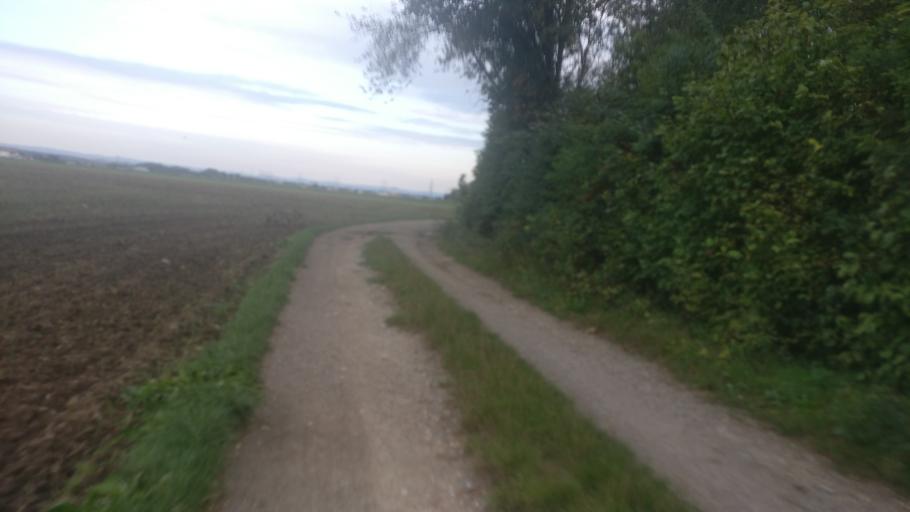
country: AT
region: Lower Austria
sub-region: Politischer Bezirk Wien-Umgebung
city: Lanzendorf
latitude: 48.1210
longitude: 16.4339
